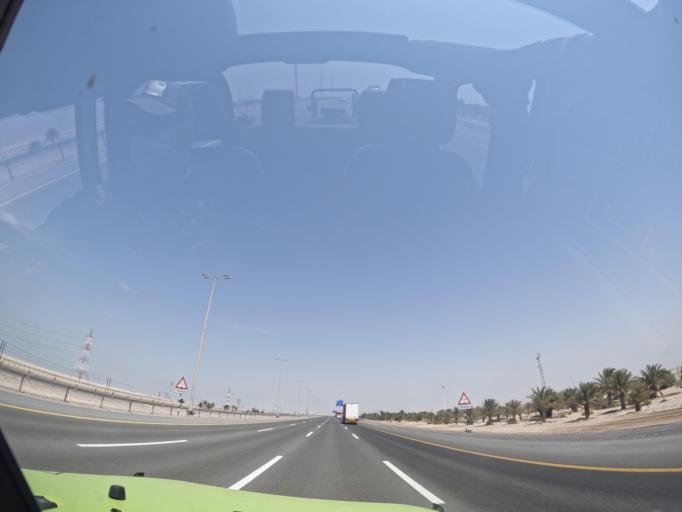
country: AE
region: Abu Dhabi
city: Abu Dhabi
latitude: 24.2048
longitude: 54.4027
